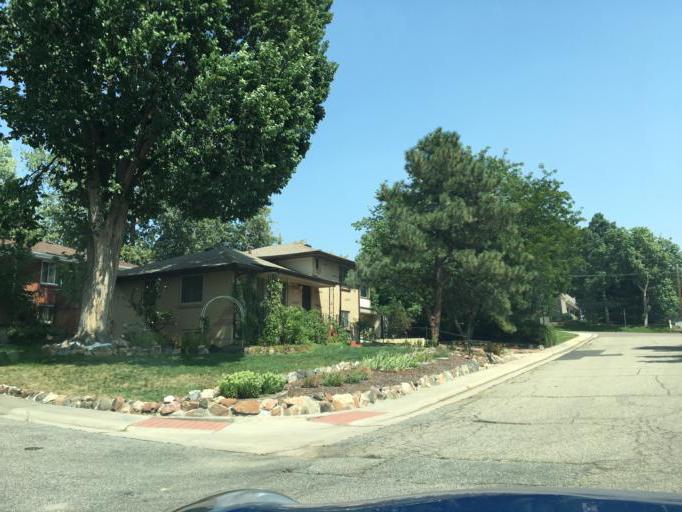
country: US
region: Colorado
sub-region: Jefferson County
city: Arvada
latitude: 39.8110
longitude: -105.0824
